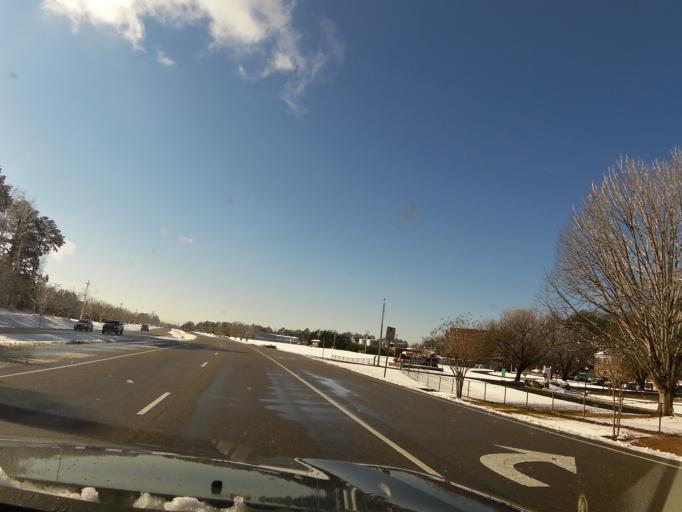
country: US
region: North Carolina
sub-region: Wilson County
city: Wilson
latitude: 35.7268
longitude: -77.8890
